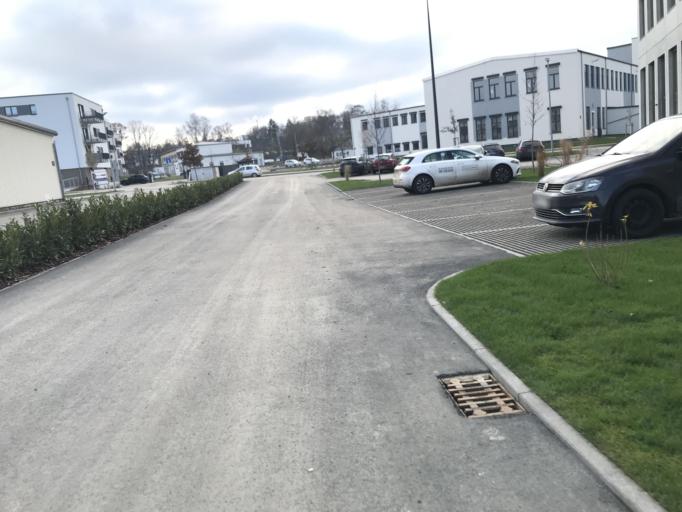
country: DE
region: Hesse
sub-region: Regierungsbezirk Giessen
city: Giessen
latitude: 50.5936
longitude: 8.7190
